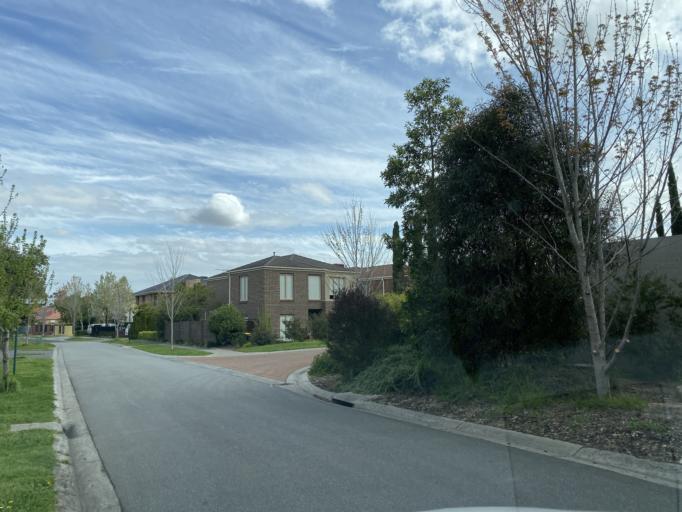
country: AU
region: Victoria
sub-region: Whitehorse
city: Surrey Hills
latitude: -37.8413
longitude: 145.1029
